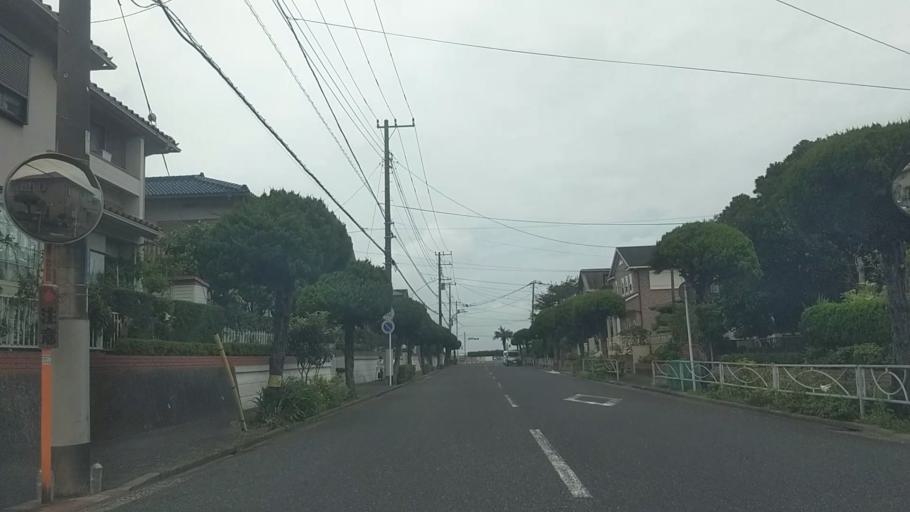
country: JP
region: Kanagawa
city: Yokosuka
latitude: 35.2620
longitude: 139.7082
